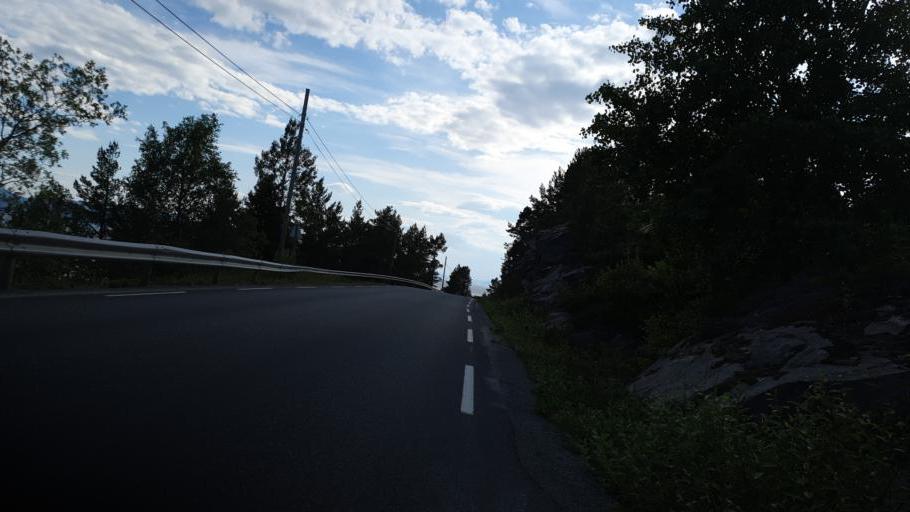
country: NO
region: Sor-Trondelag
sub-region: Trondheim
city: Trondheim
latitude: 63.5661
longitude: 10.3381
